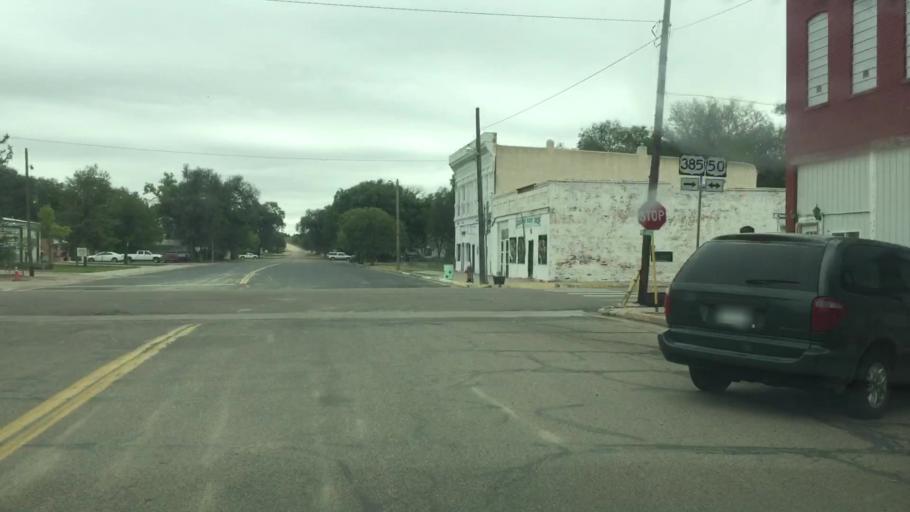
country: US
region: Colorado
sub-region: Prowers County
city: Lamar
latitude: 38.0630
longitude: -102.3104
